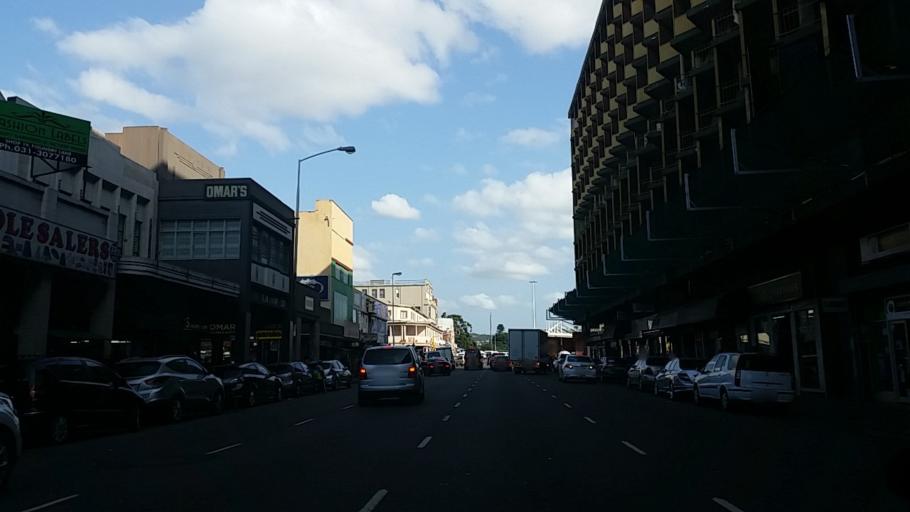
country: ZA
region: KwaZulu-Natal
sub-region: eThekwini Metropolitan Municipality
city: Durban
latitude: -29.8581
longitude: 31.0185
